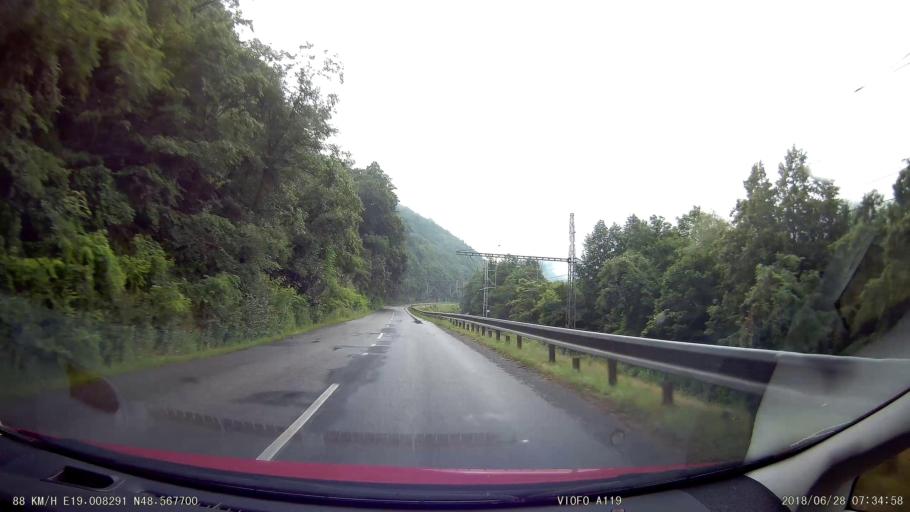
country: SK
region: Banskobystricky
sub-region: Okres Banska Bystrica
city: Zvolen
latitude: 48.5677
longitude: 19.0083
